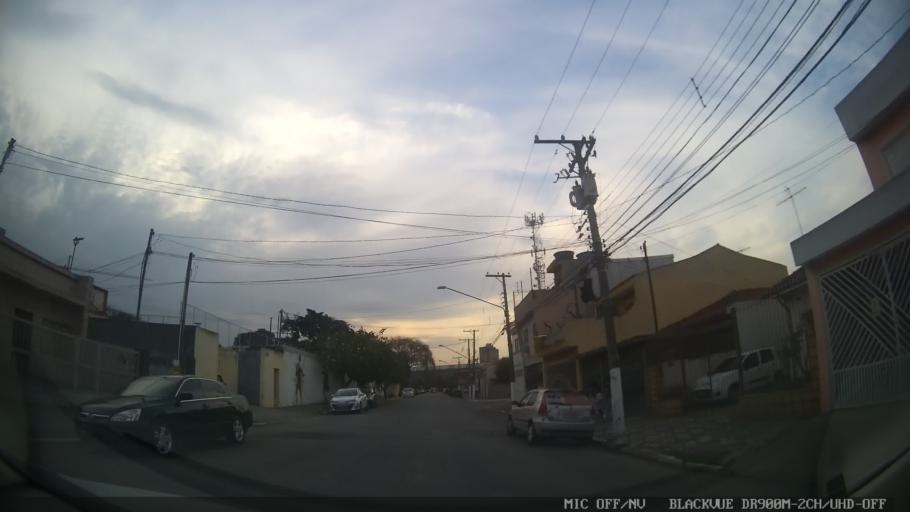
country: BR
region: Sao Paulo
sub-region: Sao Caetano Do Sul
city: Sao Caetano do Sul
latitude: -23.5975
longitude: -46.5915
